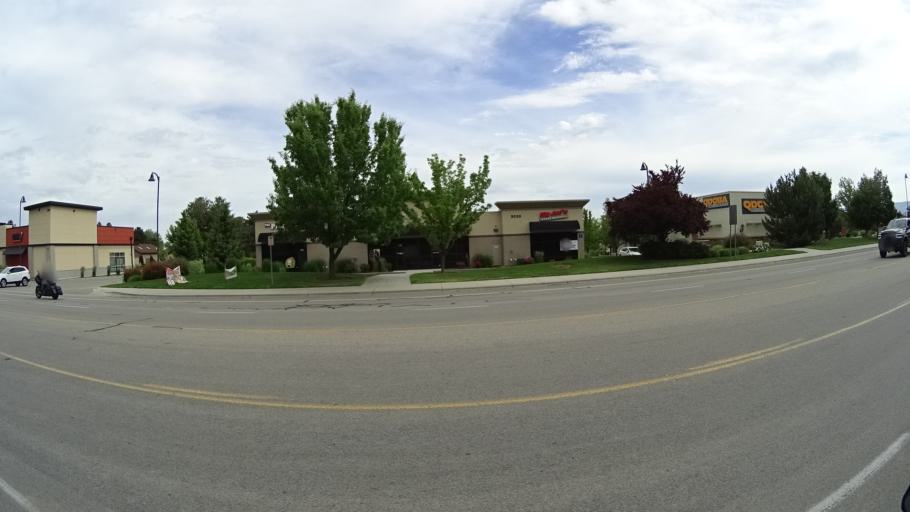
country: US
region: Idaho
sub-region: Ada County
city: Meridian
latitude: 43.5903
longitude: -116.3567
